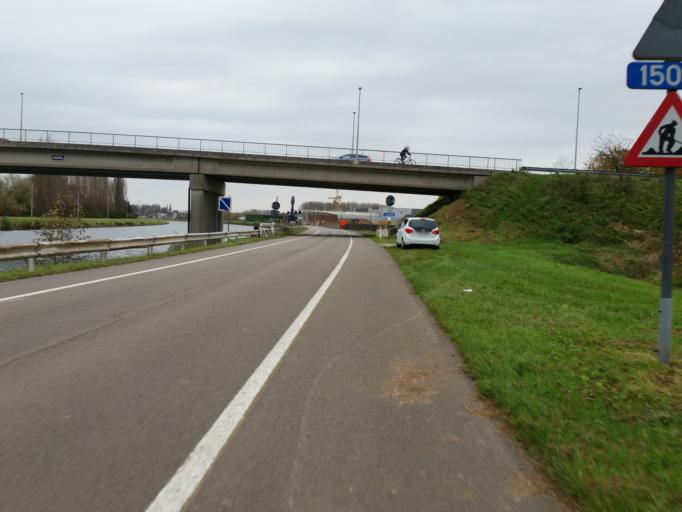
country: BE
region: Flanders
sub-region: Provincie Antwerpen
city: Lier
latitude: 51.1200
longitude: 4.5790
